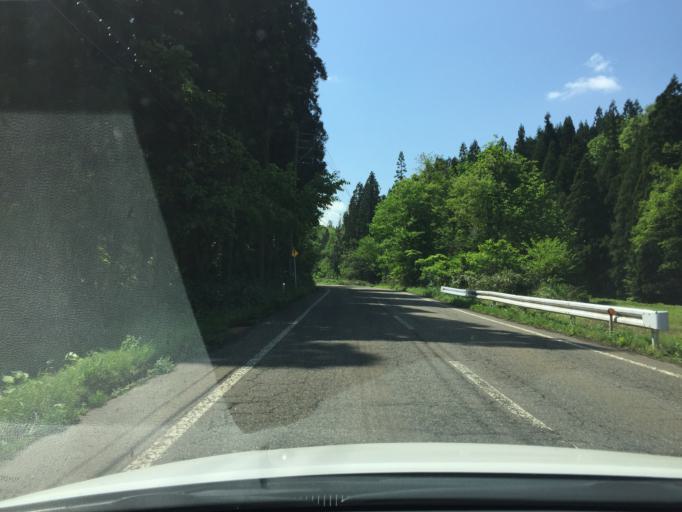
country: JP
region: Niigata
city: Tochio-honcho
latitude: 37.5375
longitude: 139.0920
